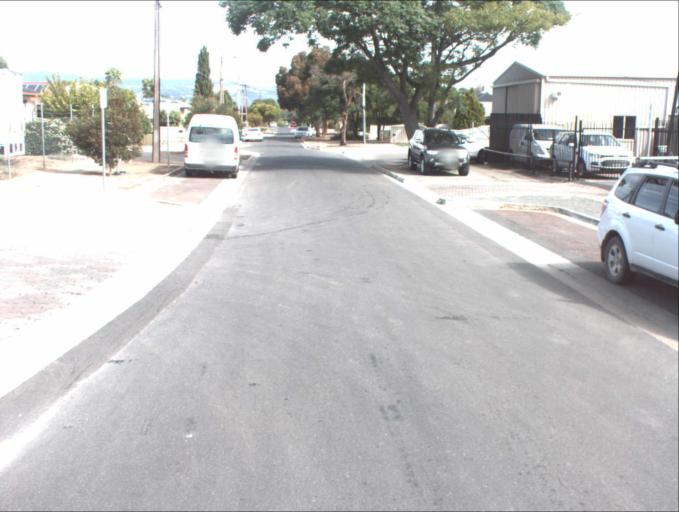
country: AU
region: South Australia
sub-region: Port Adelaide Enfield
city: Klemzig
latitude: -34.8692
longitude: 138.6400
